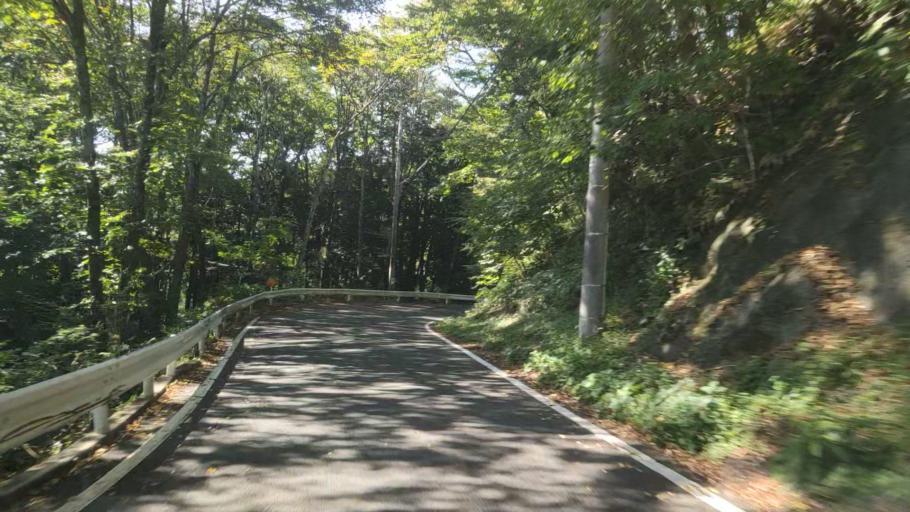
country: JP
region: Gunma
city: Nakanojomachi
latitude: 36.5988
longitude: 138.6846
